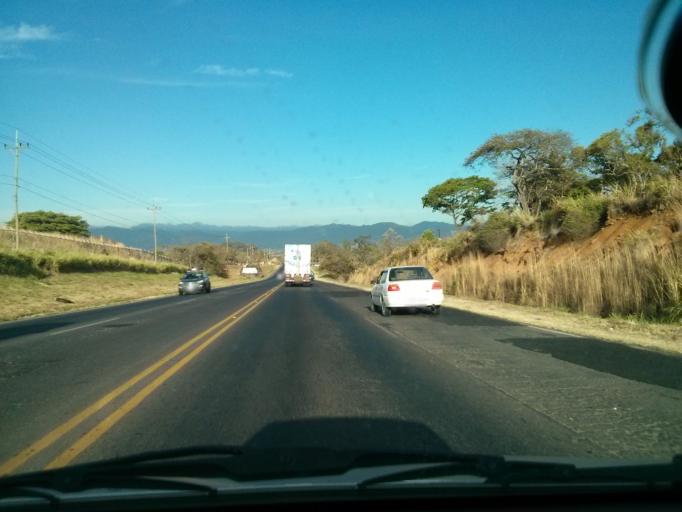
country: CR
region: Alajuela
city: Carrillos
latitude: 9.9974
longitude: -84.2730
